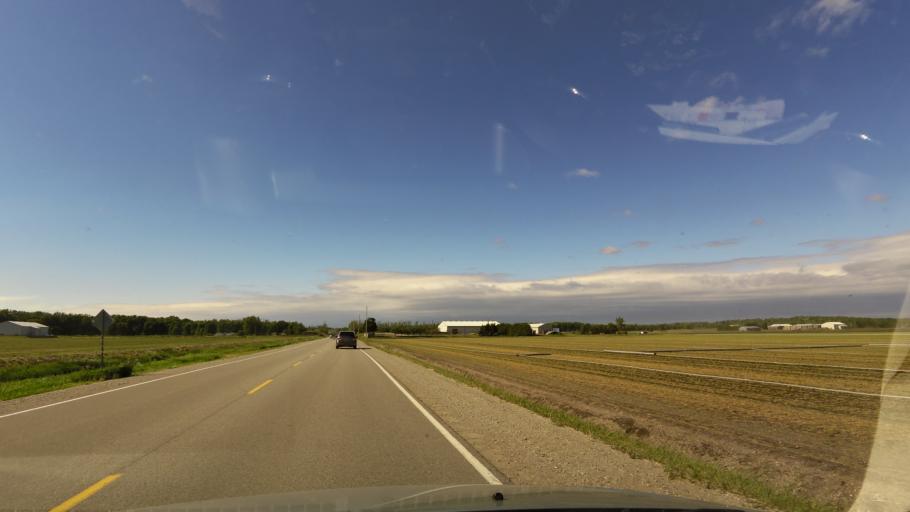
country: CA
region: Ontario
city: Innisfil
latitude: 44.2266
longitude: -79.6335
